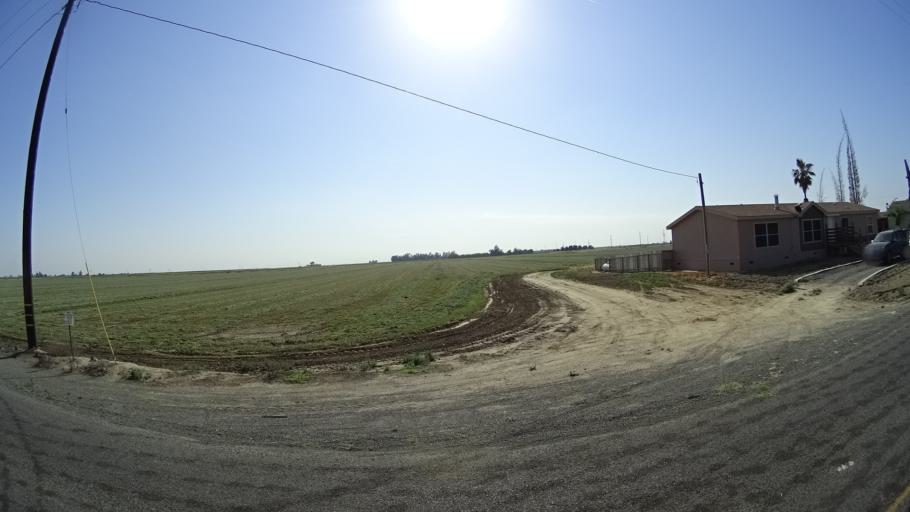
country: US
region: California
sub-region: Kings County
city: Home Garden
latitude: 36.3005
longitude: -119.5831
